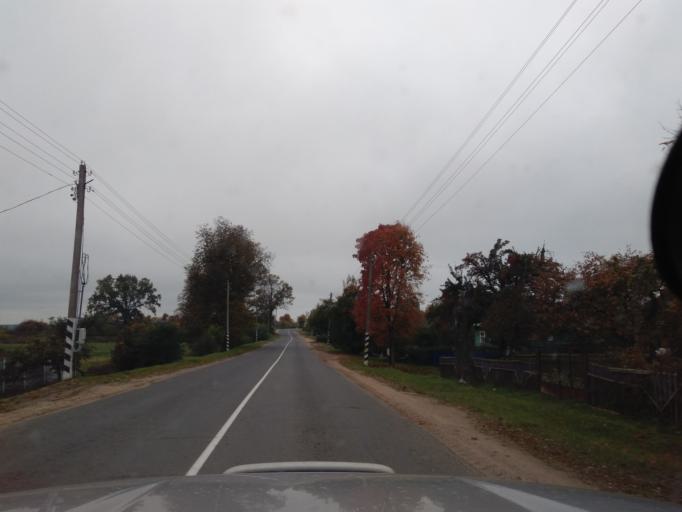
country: BY
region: Minsk
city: Kapyl'
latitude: 53.1522
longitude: 27.1526
